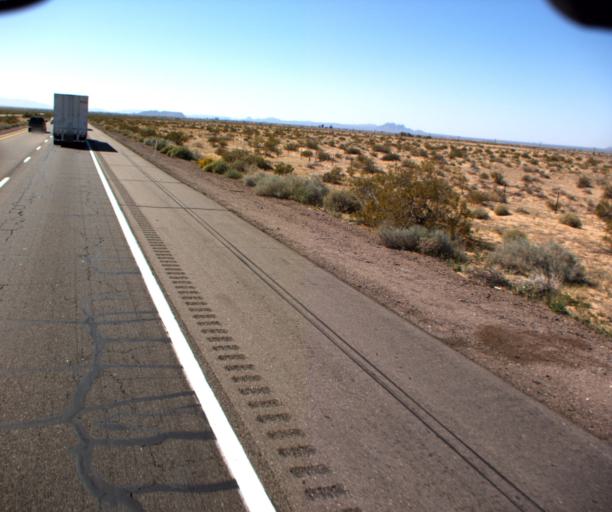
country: US
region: Arizona
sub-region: Yuma County
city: Wellton
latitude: 32.7128
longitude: -113.8278
